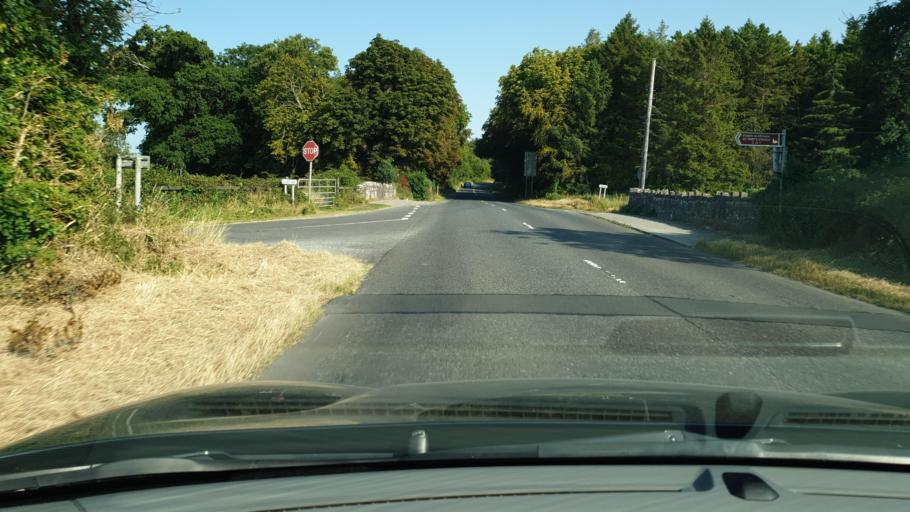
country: IE
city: Kentstown
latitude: 53.6257
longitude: -6.5251
